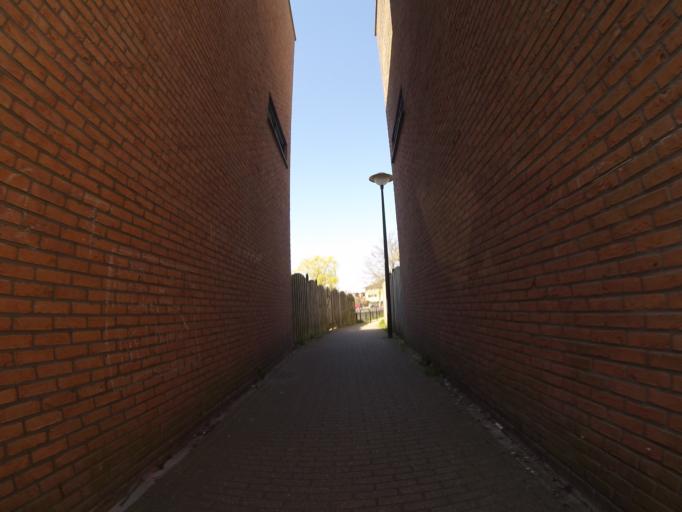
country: NL
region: Utrecht
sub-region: Gemeente Amersfoort
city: Hoogland
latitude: 52.2019
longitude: 5.3798
